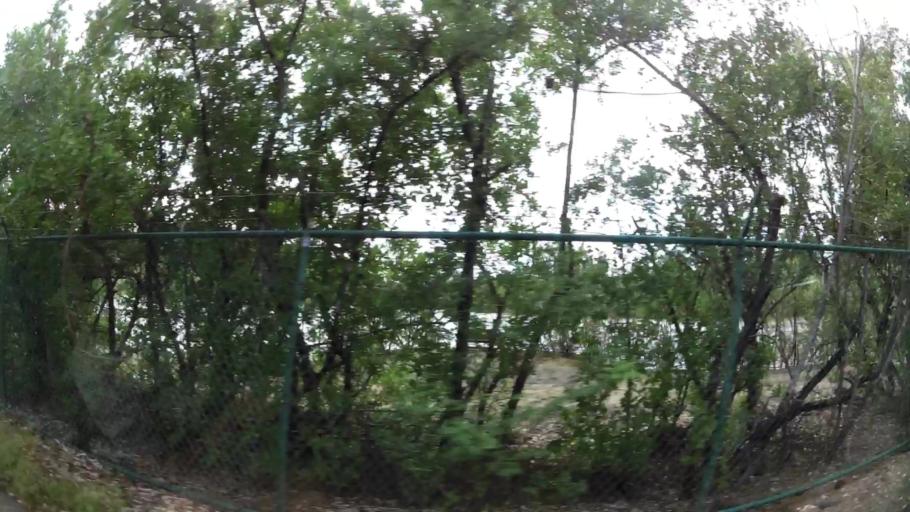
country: AG
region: Saint John
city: Saint John's
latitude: 17.1211
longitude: -61.8907
